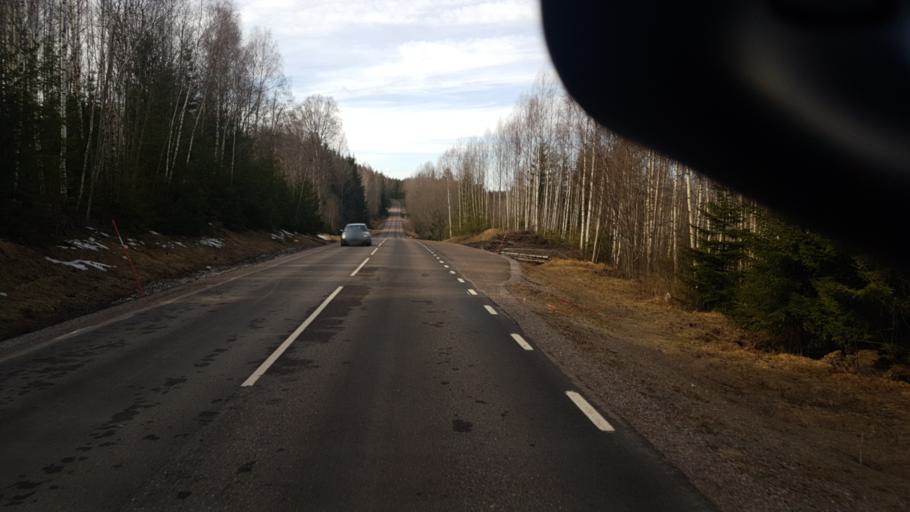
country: SE
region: Vaermland
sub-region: Eda Kommun
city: Amotfors
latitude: 59.7318
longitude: 12.4168
